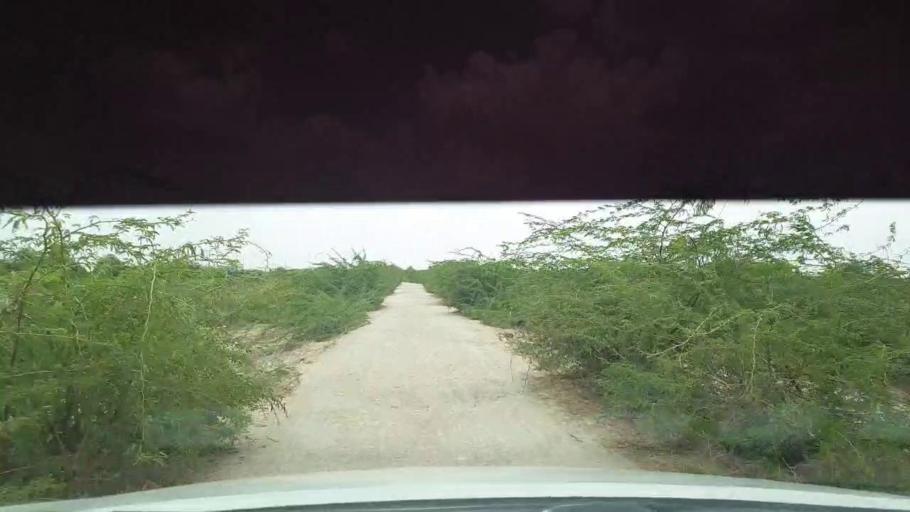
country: PK
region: Sindh
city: Kadhan
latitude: 24.4647
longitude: 69.0394
